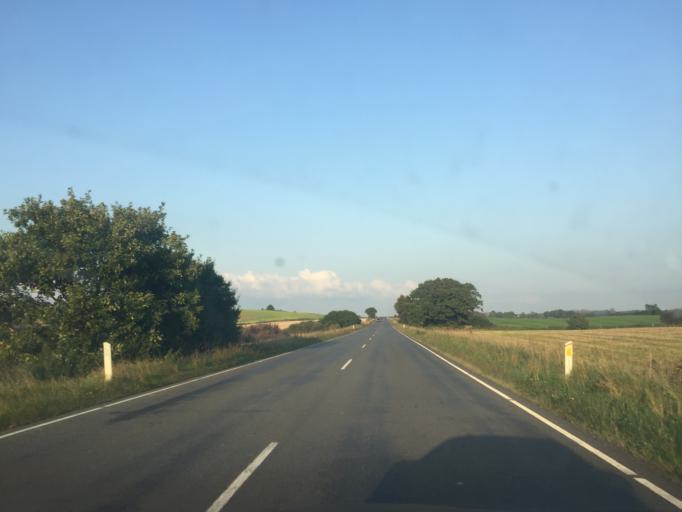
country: DK
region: Zealand
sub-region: Soro Kommune
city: Stenlille
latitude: 55.5309
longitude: 11.5555
